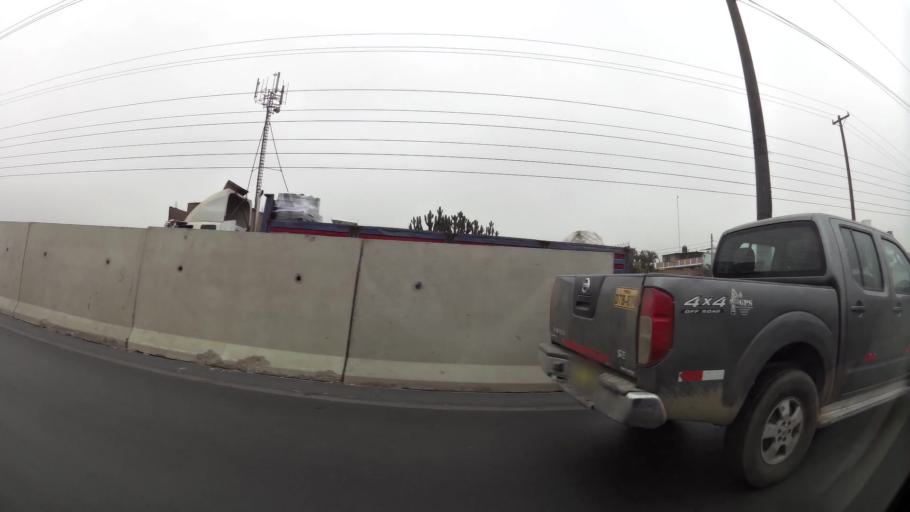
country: PE
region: Lima
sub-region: Lima
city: Urb. Santo Domingo
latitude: -11.8892
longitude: -77.0684
